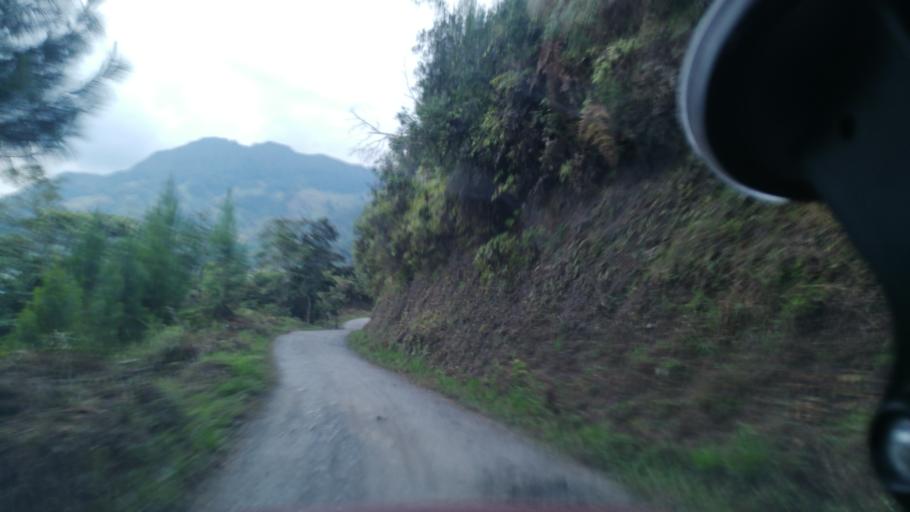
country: CO
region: Cundinamarca
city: Vergara
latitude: 5.1659
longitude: -74.2618
